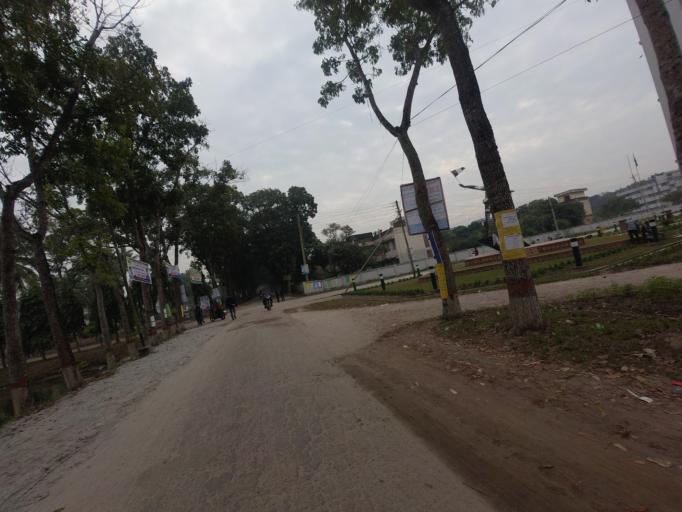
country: BD
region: Barisal
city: Nalchiti
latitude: 22.4643
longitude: 90.3822
